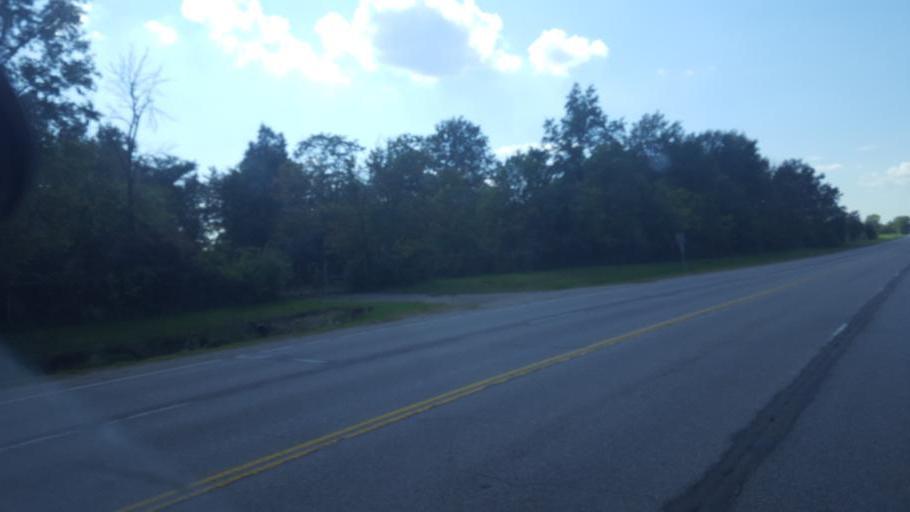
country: US
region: Ohio
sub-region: Franklin County
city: Grove City
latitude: 39.8925
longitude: -83.0964
